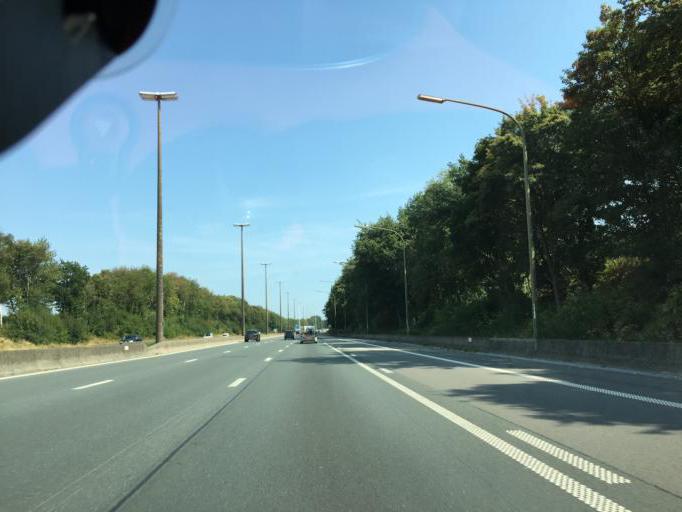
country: BE
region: Wallonia
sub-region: Province du Hainaut
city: Brunehault
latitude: 50.4810
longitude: 4.4558
